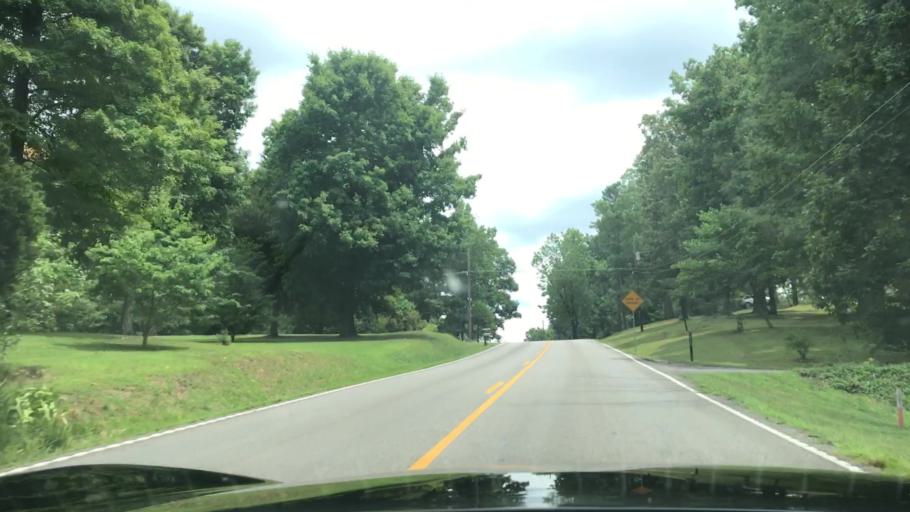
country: US
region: Kentucky
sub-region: Muhlenberg County
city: Greenville
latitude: 37.2034
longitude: -87.0848
